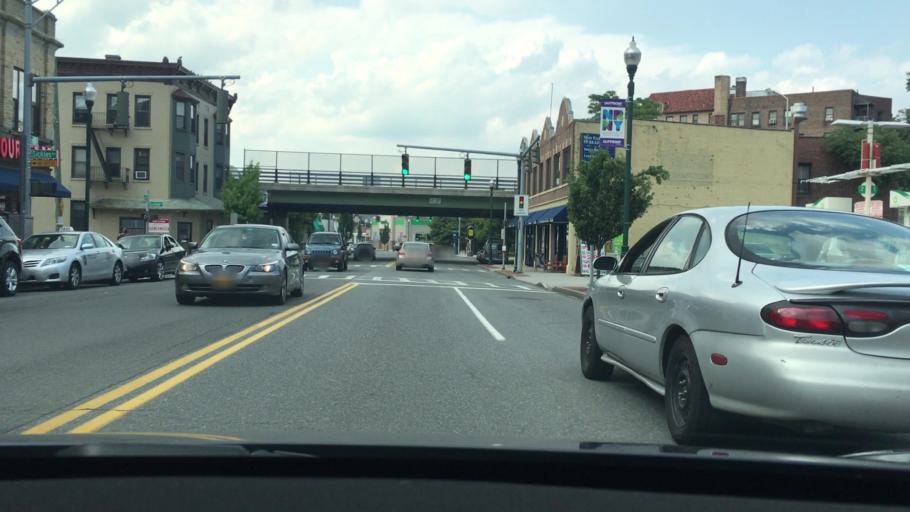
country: US
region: New York
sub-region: Westchester County
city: New Rochelle
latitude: 40.9154
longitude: -73.7849
